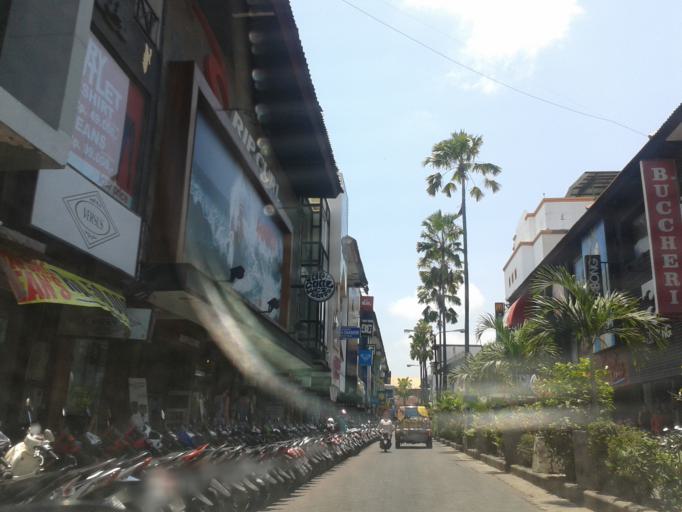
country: ID
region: Bali
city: Kuta
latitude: -8.7243
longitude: 115.1712
